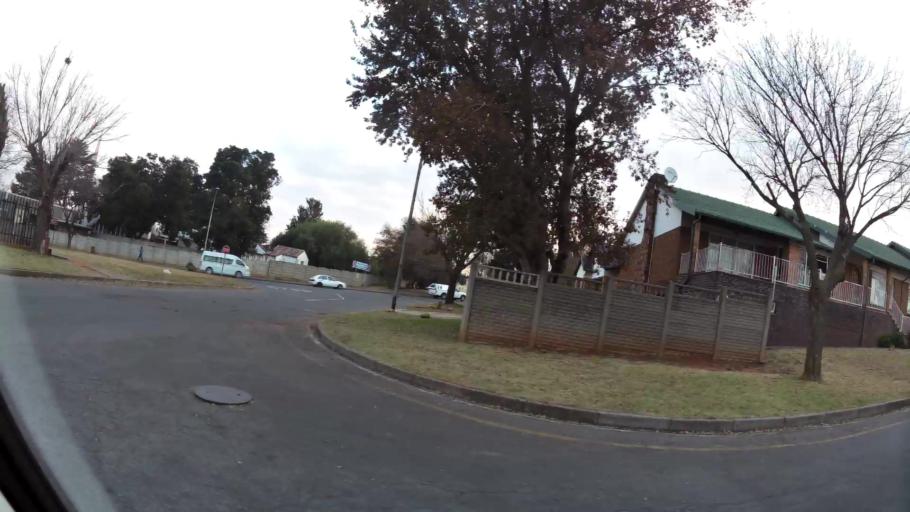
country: ZA
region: Gauteng
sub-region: Ekurhuleni Metropolitan Municipality
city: Germiston
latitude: -26.1838
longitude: 28.1582
